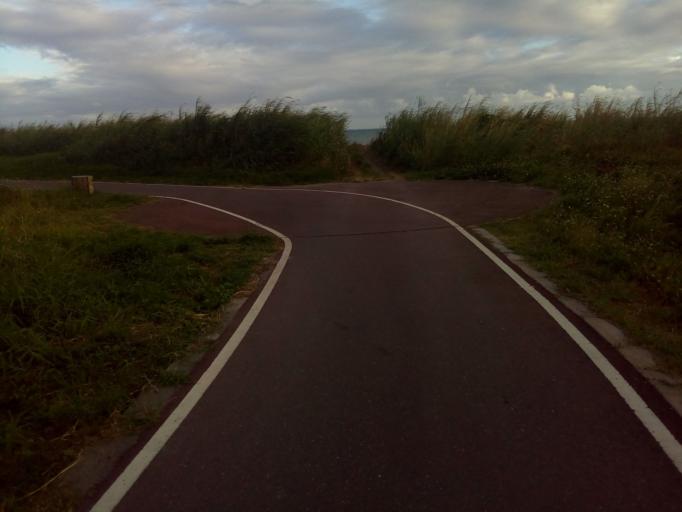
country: TW
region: Taiwan
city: Taitung City
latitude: 22.7506
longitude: 121.1596
